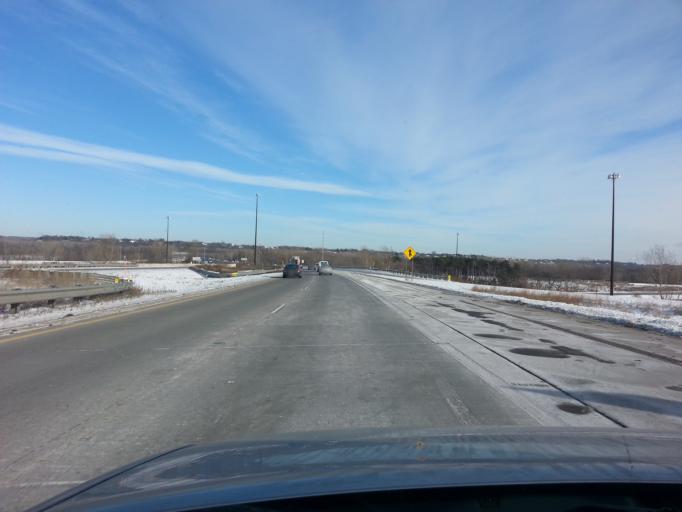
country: US
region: Minnesota
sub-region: Scott County
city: Savage
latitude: 44.7880
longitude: -93.4082
